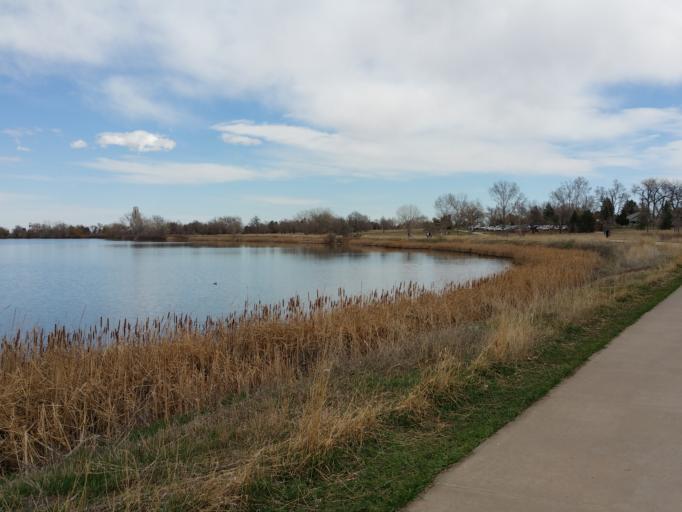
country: US
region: Colorado
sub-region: Jefferson County
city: Wheat Ridge
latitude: 39.7558
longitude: -105.1058
